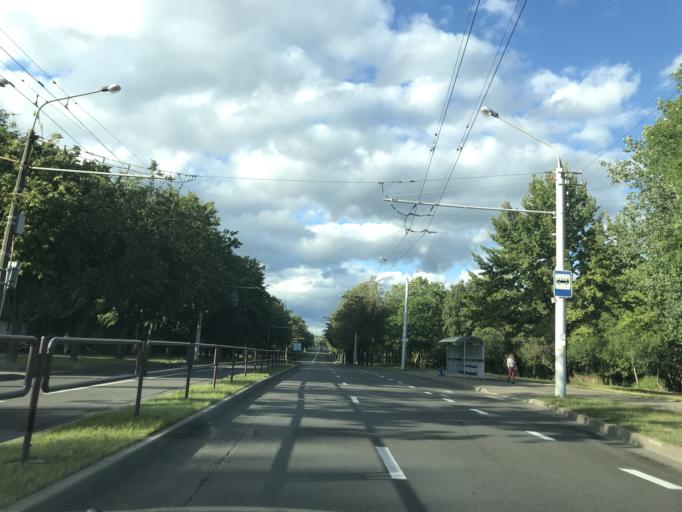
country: BY
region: Minsk
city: Minsk
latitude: 53.9399
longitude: 27.6170
